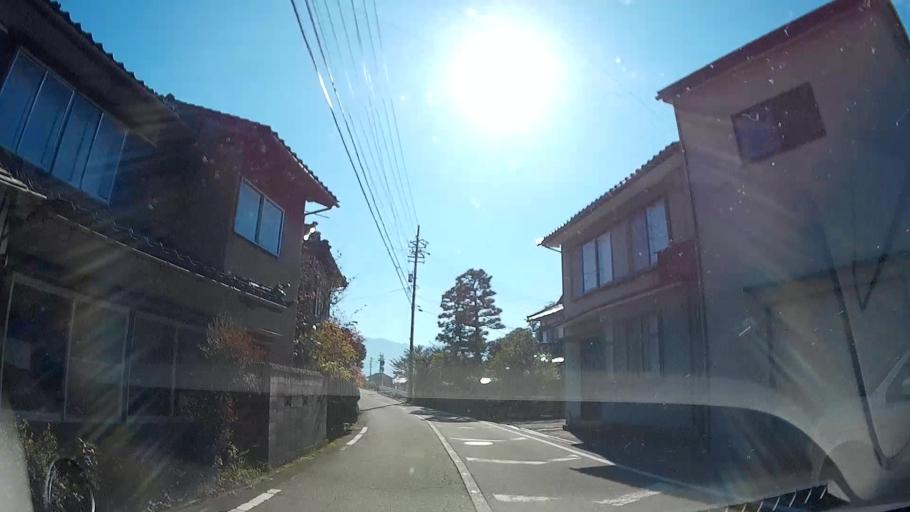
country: JP
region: Toyama
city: Fukumitsu
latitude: 36.5529
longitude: 136.8715
